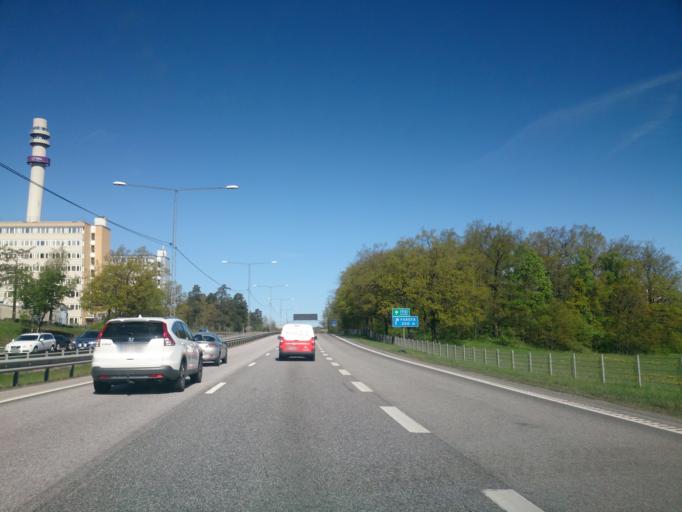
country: SE
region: Stockholm
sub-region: Stockholms Kommun
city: Arsta
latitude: 59.2452
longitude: 18.1047
